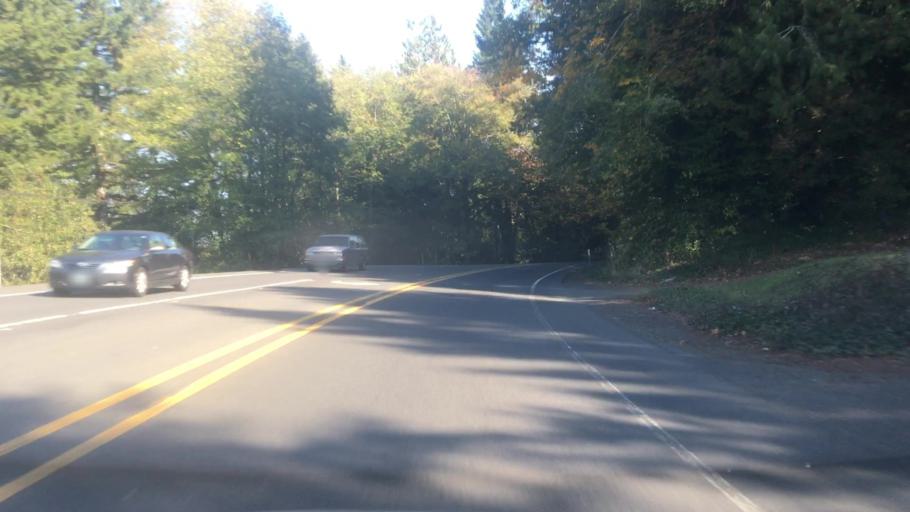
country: US
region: Oregon
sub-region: Lincoln County
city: Rose Lodge
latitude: 45.0117
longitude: -123.8787
